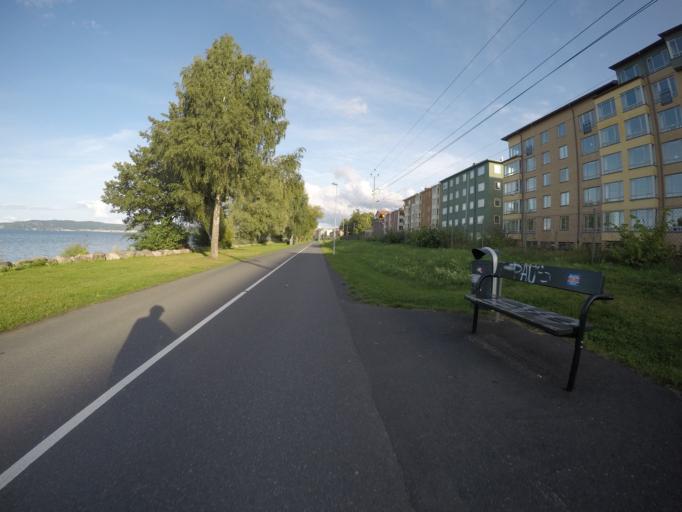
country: SE
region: Joenkoeping
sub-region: Jonkopings Kommun
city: Jonkoping
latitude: 57.7832
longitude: 14.1756
